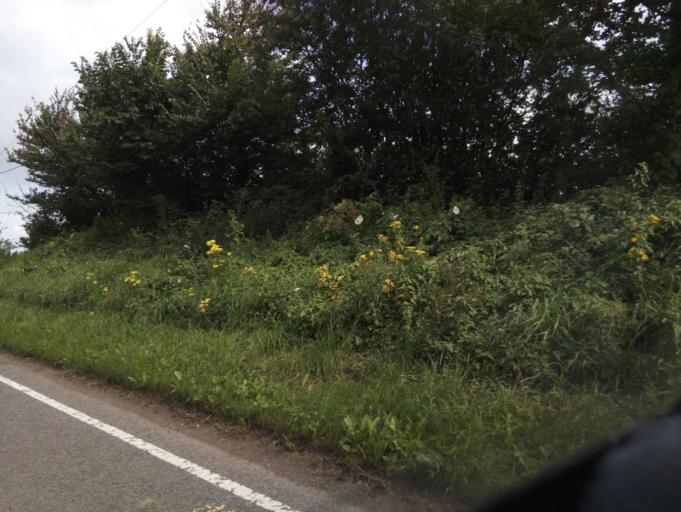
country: GB
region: England
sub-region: Dorset
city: Stalbridge
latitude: 50.9959
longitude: -2.4138
